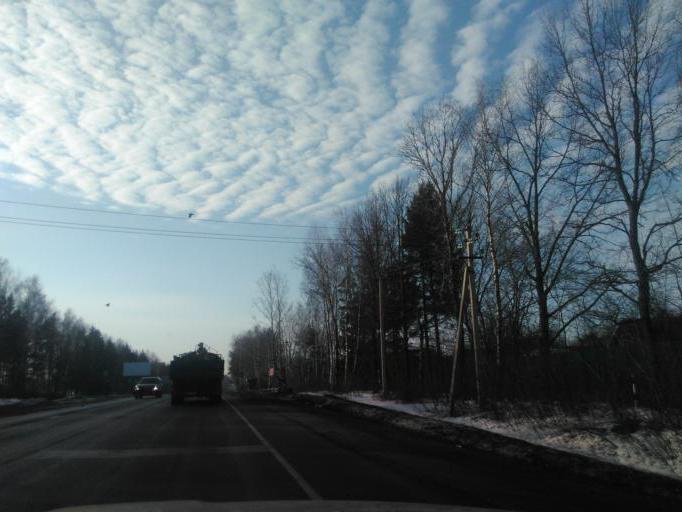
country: RU
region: Moskovskaya
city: Snegiri
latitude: 55.8810
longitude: 36.9438
